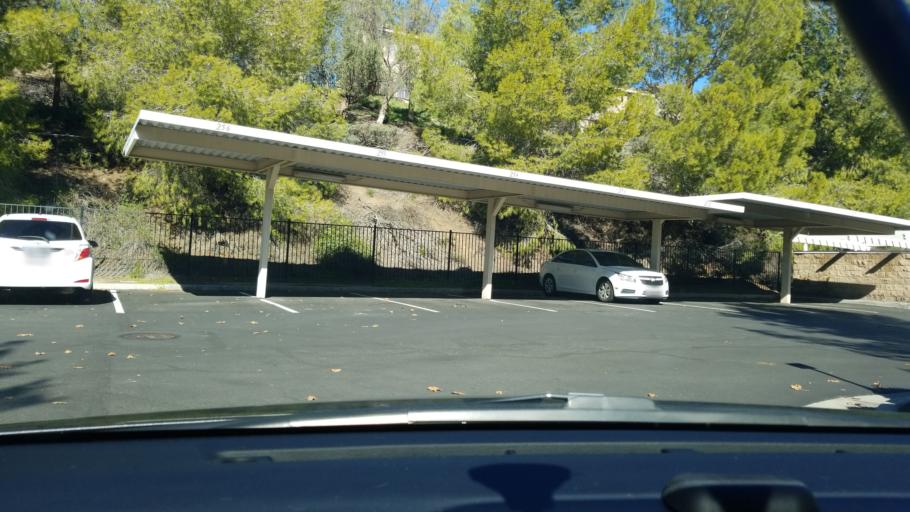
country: US
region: California
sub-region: Riverside County
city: Temecula
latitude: 33.5104
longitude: -117.1350
